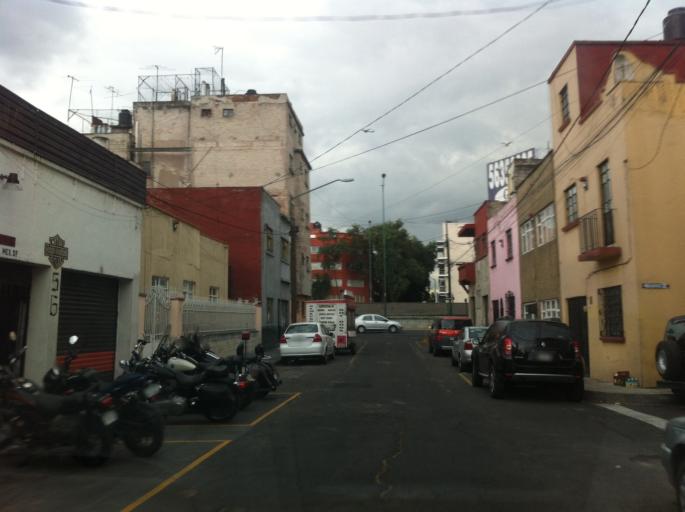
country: MX
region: Mexico City
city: Benito Juarez
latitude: 19.4034
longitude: -99.1615
